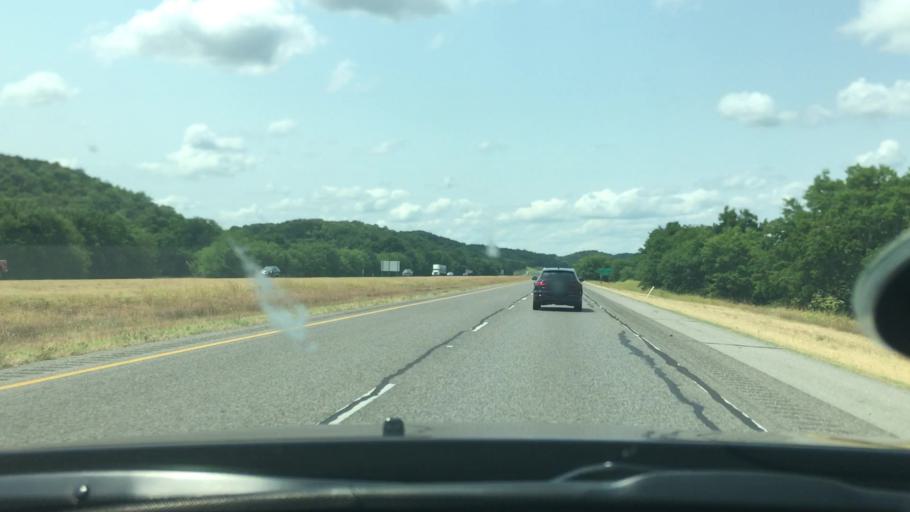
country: US
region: Oklahoma
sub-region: Murray County
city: Davis
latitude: 34.4585
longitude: -97.1425
